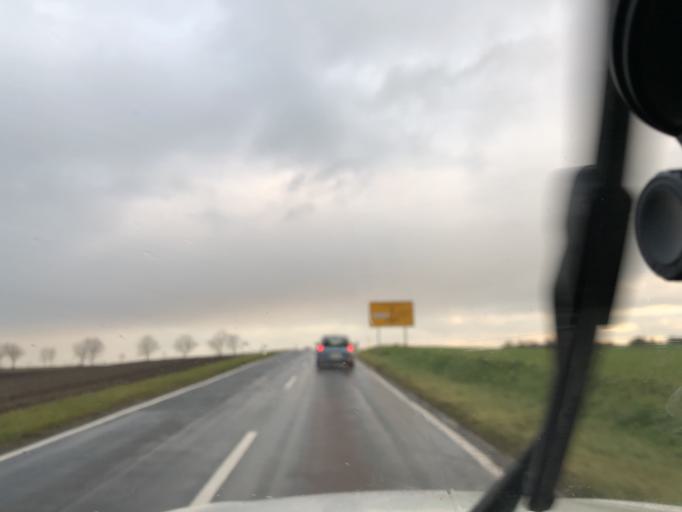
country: DE
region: Saxony-Anhalt
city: Teutschenthal
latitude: 51.4610
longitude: 11.7853
